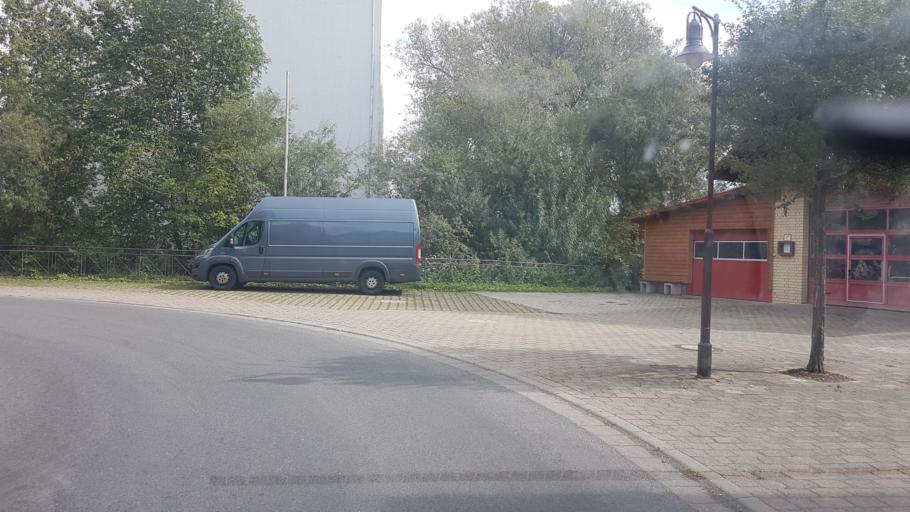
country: DE
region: Bavaria
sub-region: Upper Franconia
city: Grossheirath
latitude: 50.1974
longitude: 10.9522
